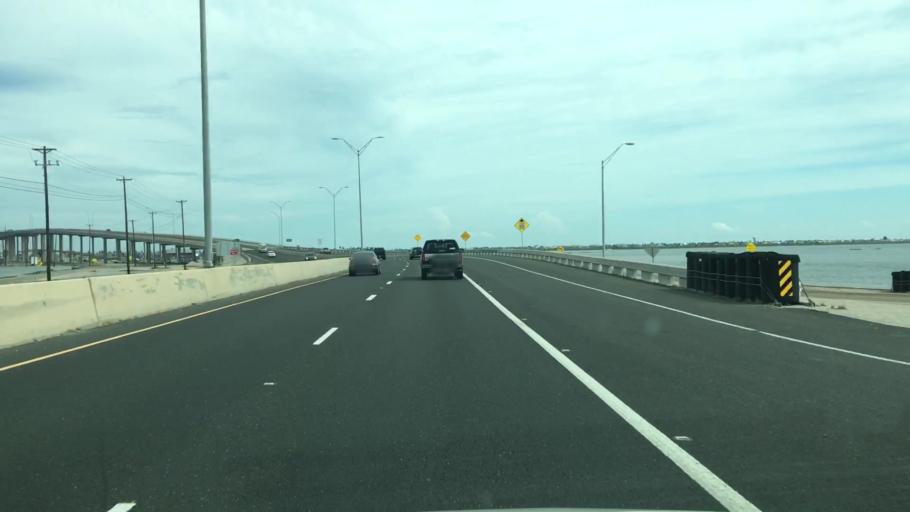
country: US
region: Texas
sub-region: Nueces County
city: Corpus Christi
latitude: 27.6391
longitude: -97.2463
